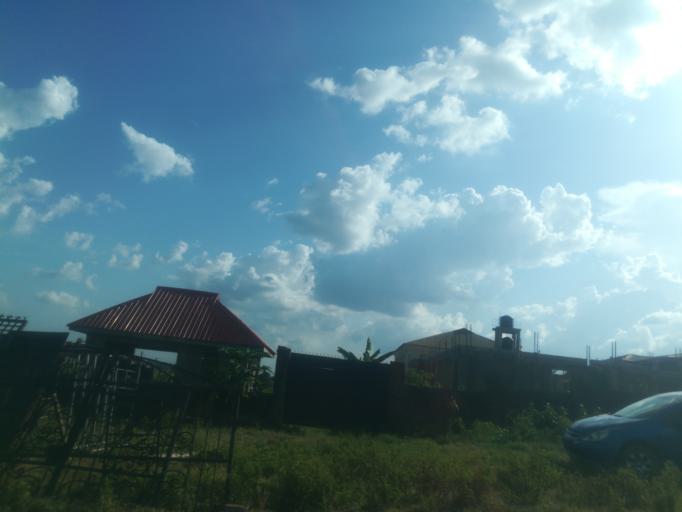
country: NG
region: Oyo
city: Ibadan
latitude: 7.4382
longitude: 3.9671
